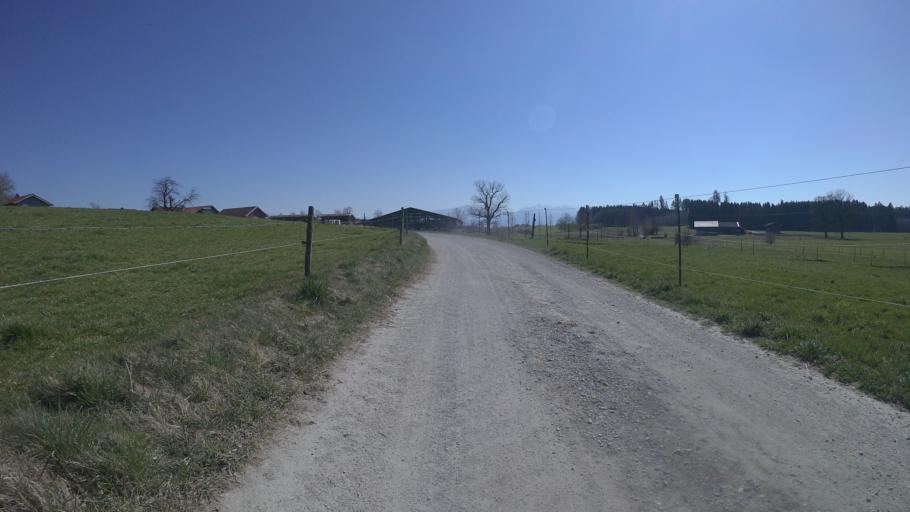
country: DE
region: Bavaria
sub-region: Upper Bavaria
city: Chieming
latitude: 47.9228
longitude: 12.5251
